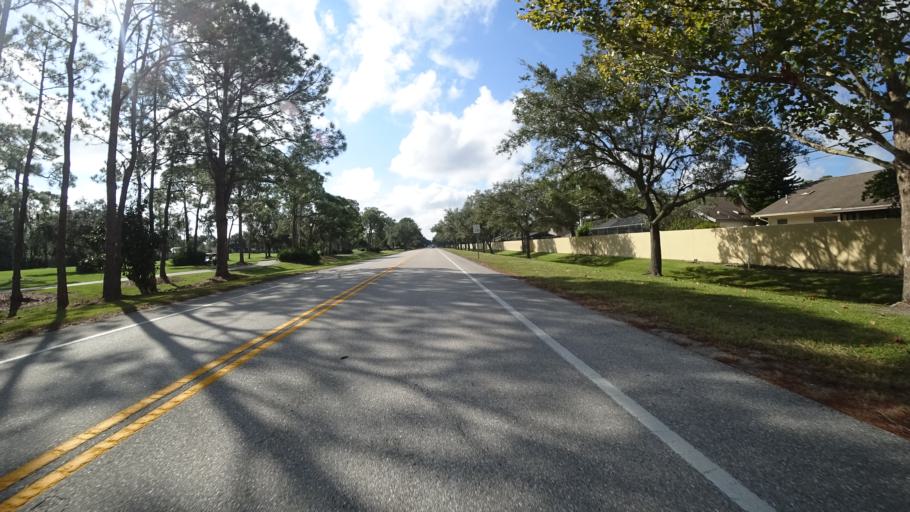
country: US
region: Florida
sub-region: Sarasota County
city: Desoto Lakes
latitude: 27.4031
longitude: -82.4871
